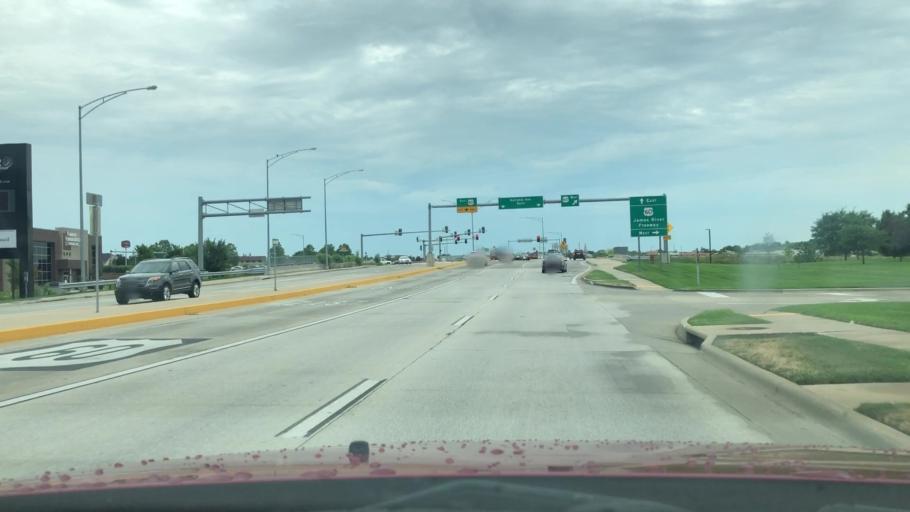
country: US
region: Missouri
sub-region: Greene County
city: Springfield
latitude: 37.1446
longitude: -93.2782
